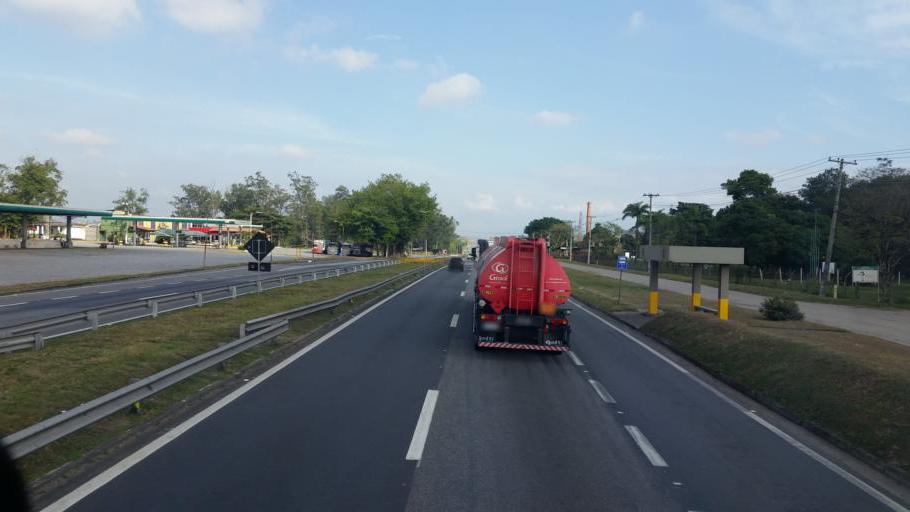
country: BR
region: Rio de Janeiro
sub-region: Resende
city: Resende
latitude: -22.4558
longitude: -44.3975
